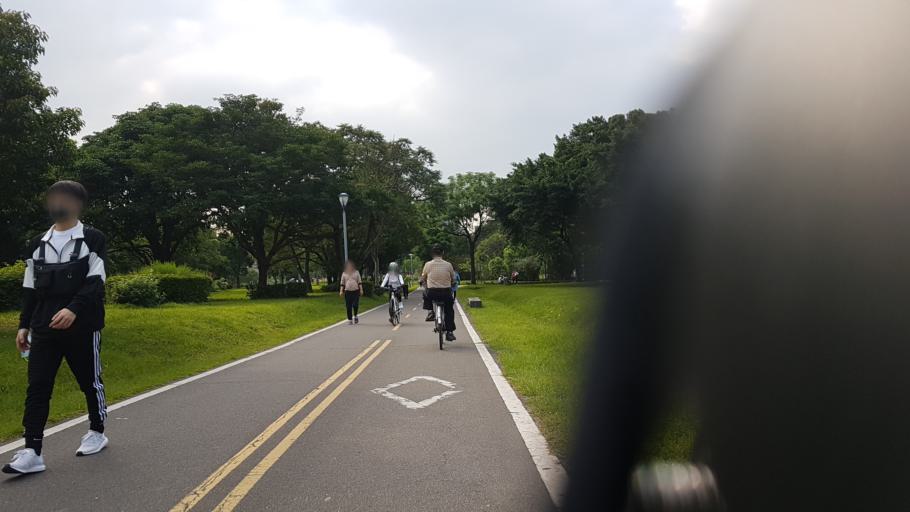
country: TW
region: Taipei
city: Taipei
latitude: 25.0181
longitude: 121.5233
